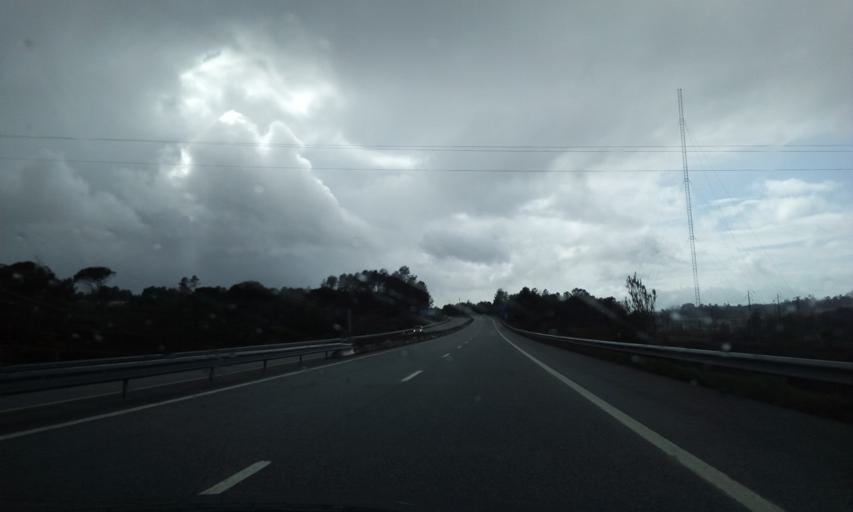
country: PT
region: Viseu
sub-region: Viseu
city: Viseu
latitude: 40.6288
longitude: -7.8955
